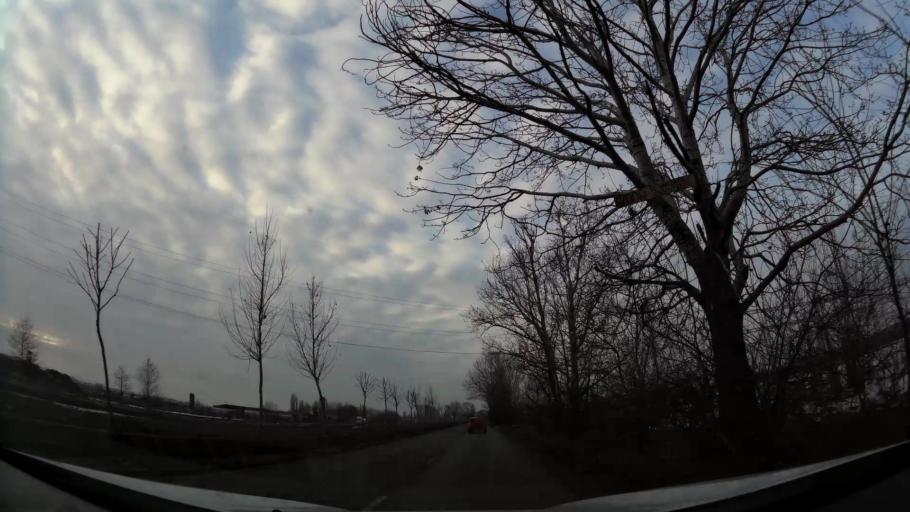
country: RO
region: Ilfov
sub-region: Comuna Popesti-Leordeni
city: Popesti-Leordeni
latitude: 44.3953
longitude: 26.1762
